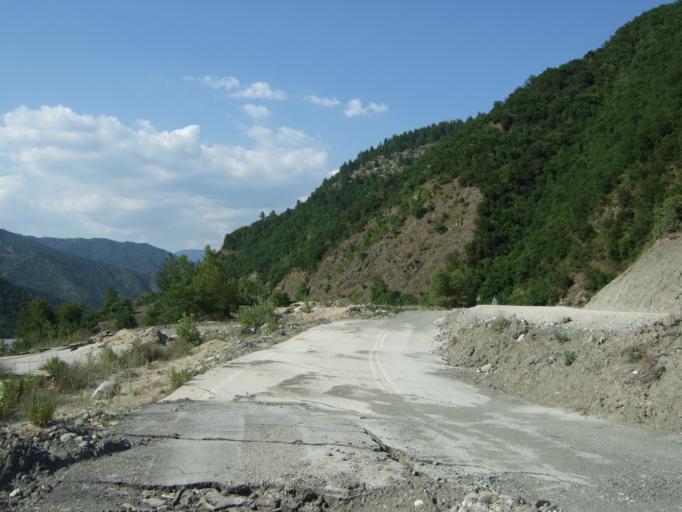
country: GR
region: Epirus
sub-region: Nomos Ioanninon
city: Konitsa
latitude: 40.1707
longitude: 20.8024
